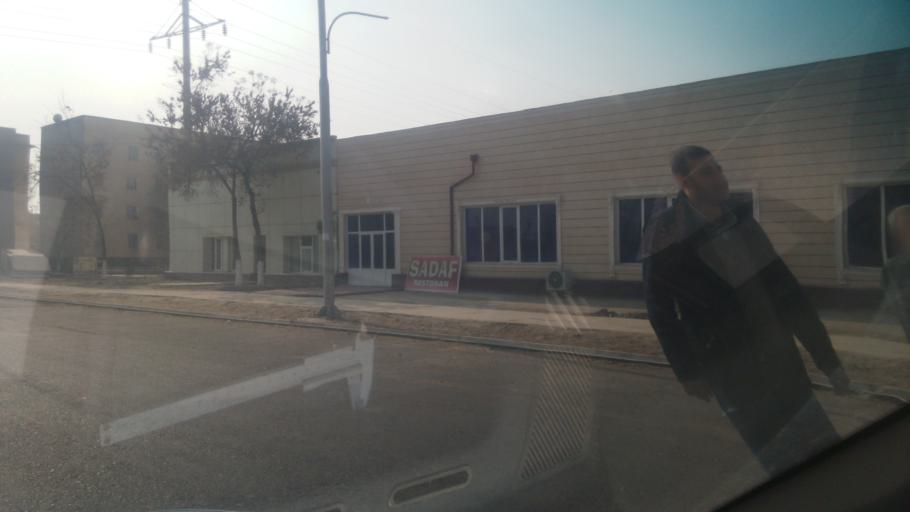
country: UZ
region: Sirdaryo
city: Guliston
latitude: 40.5053
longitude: 68.7743
